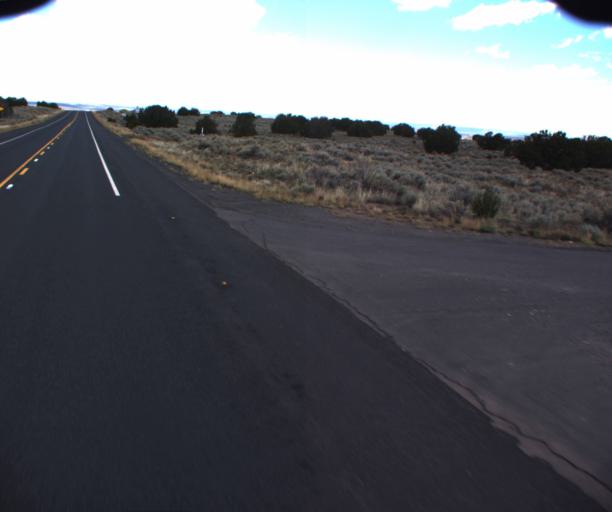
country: US
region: Arizona
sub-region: Apache County
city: Houck
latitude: 35.1713
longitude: -109.3382
